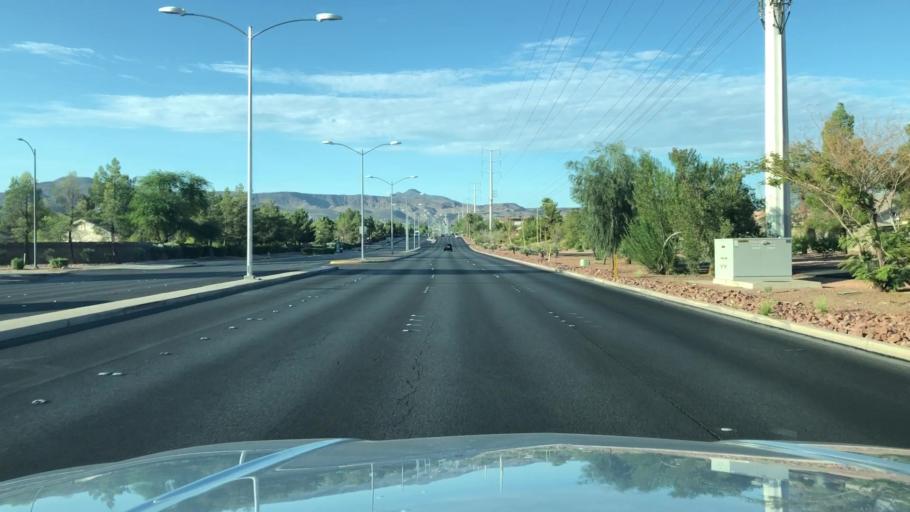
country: US
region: Nevada
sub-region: Clark County
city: Whitney
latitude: 36.0530
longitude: -115.0465
